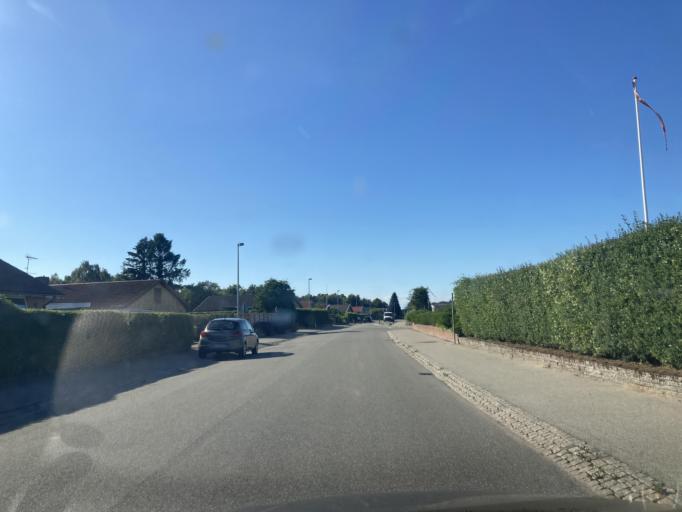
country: DK
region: Capital Region
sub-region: Halsnaes Kommune
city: Frederiksvaerk
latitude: 55.9826
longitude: 12.0070
